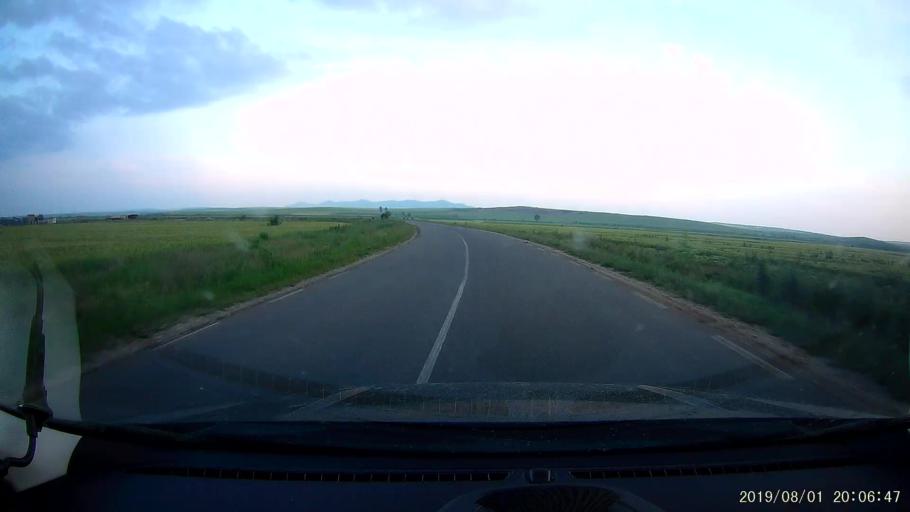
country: BG
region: Yambol
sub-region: Obshtina Yambol
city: Yambol
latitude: 42.5309
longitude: 26.5579
